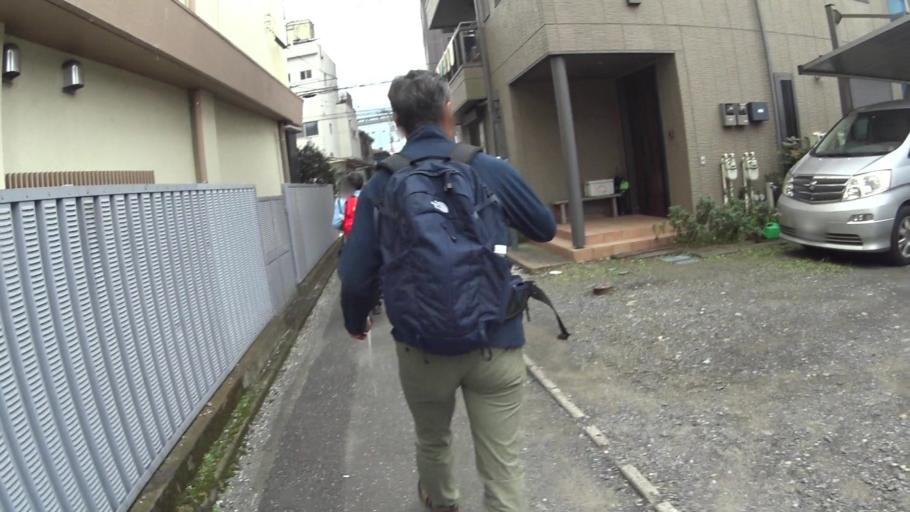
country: JP
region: Saitama
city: Hanno
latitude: 35.8537
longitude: 139.3205
